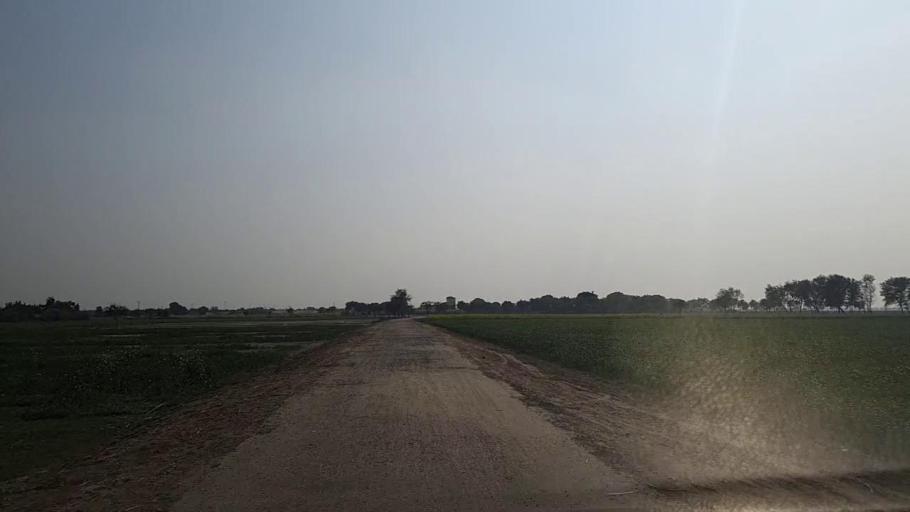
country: PK
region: Sindh
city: Daur
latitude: 26.4030
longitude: 68.4176
